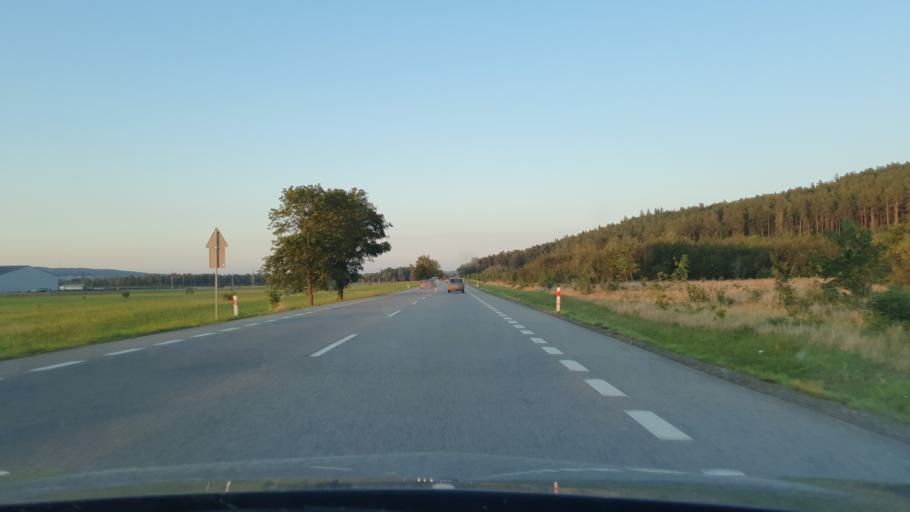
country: PL
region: Pomeranian Voivodeship
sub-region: Powiat leborski
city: Nowa Wies Leborska
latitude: 54.5157
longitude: 17.6773
